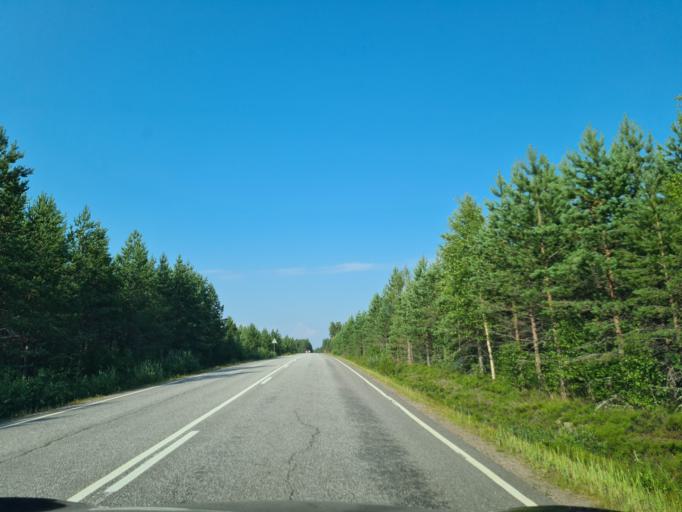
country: FI
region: Satakunta
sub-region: Pohjois-Satakunta
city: Karvia
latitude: 62.2945
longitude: 22.6220
